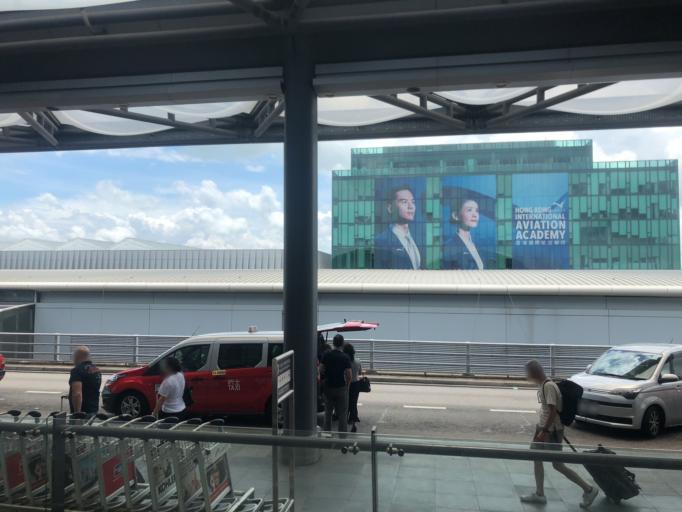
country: HK
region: Tuen Mun
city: Tuen Mun
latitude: 22.3146
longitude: 113.9366
